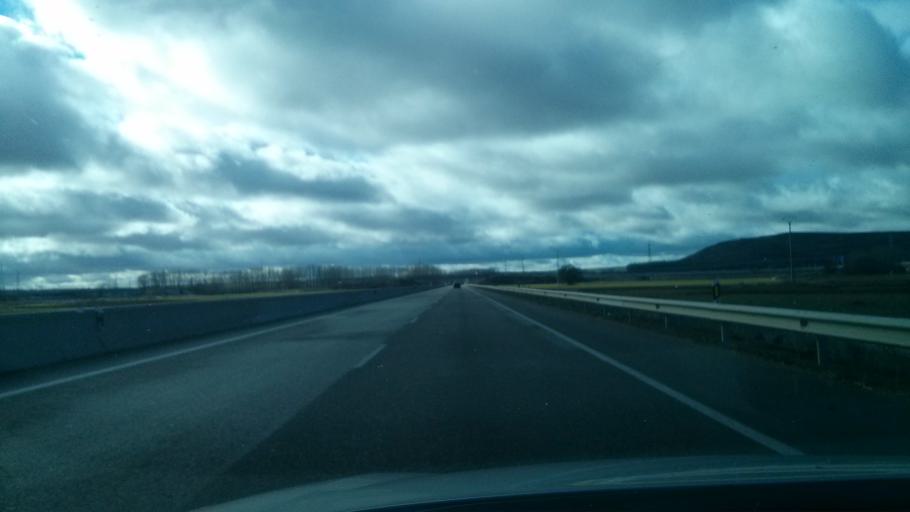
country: ES
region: Castille and Leon
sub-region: Provincia de Burgos
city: Villalbilla de Burgos
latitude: 42.3556
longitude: -3.7784
